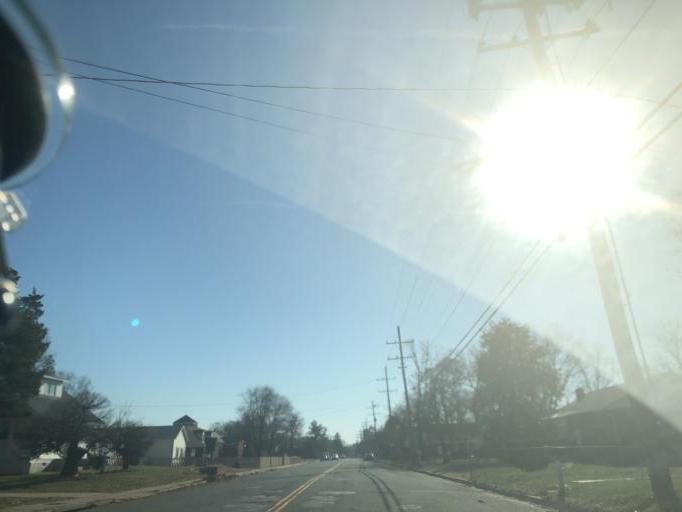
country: US
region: Virginia
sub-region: Fairfax County
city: Baileys Crossroads
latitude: 38.8462
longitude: -77.1353
